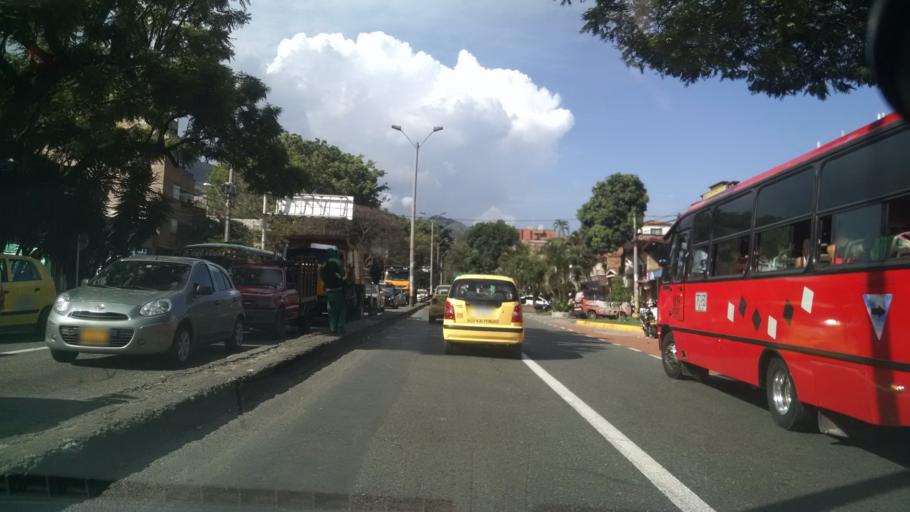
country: CO
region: Antioquia
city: Medellin
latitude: 6.2643
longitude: -75.5965
